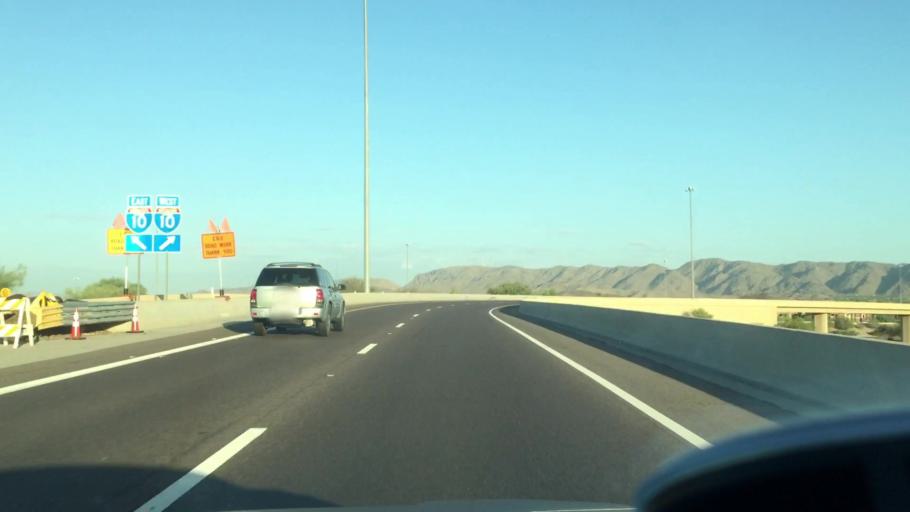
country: US
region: Arizona
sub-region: Maricopa County
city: Guadalupe
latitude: 33.2940
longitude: -111.9739
